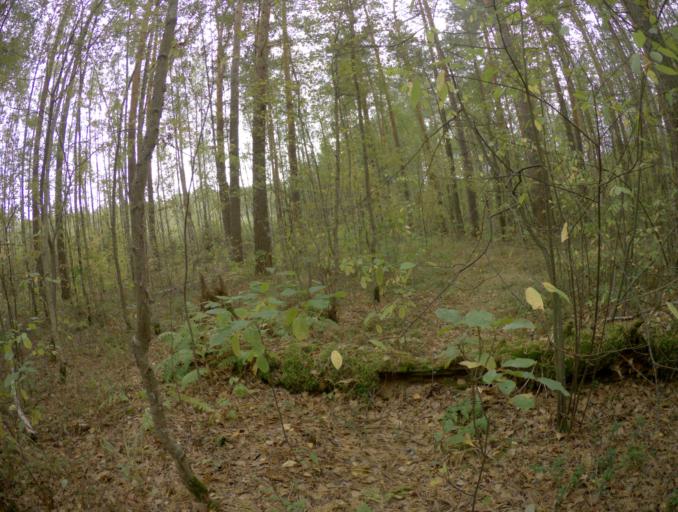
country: RU
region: Vladimir
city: Kommunar
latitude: 56.1309
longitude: 40.4957
